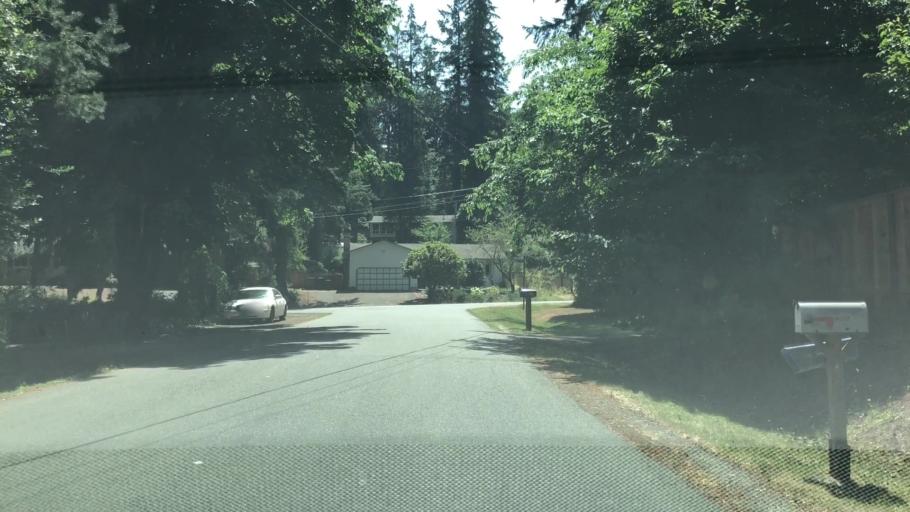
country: US
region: Washington
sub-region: King County
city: Cottage Lake
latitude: 47.7413
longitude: -122.0995
